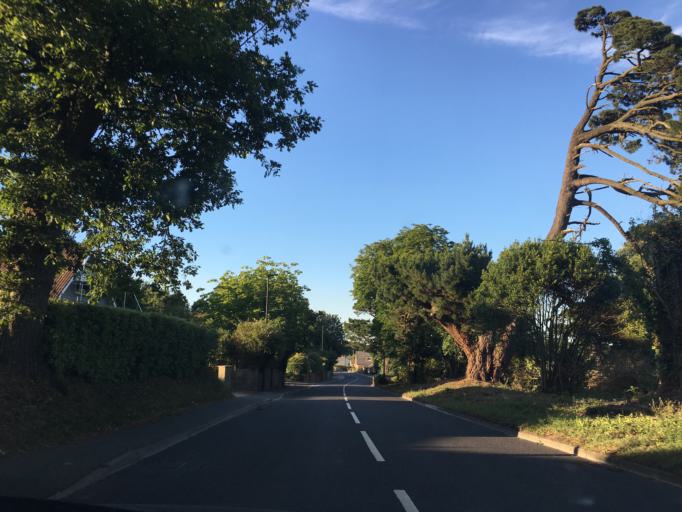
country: GB
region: England
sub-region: Isle of Wight
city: Newport
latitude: 50.7183
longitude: -1.2435
